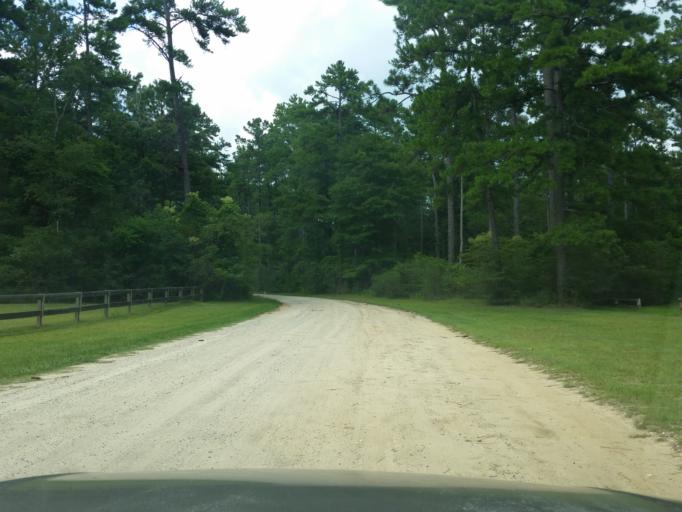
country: US
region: Alabama
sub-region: Baldwin County
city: Spanish Fort
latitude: 30.7424
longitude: -87.9153
